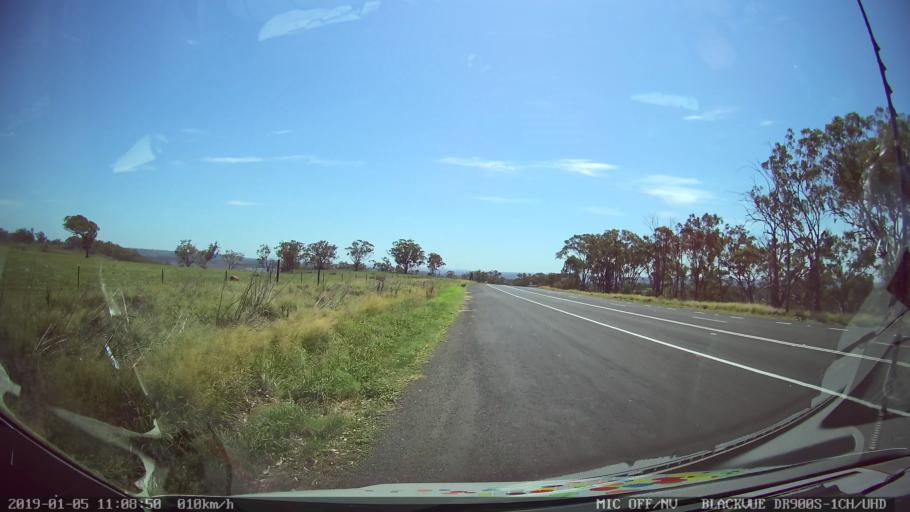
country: AU
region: New South Wales
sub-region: Warrumbungle Shire
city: Coonabarabran
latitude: -31.4142
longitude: 149.2305
